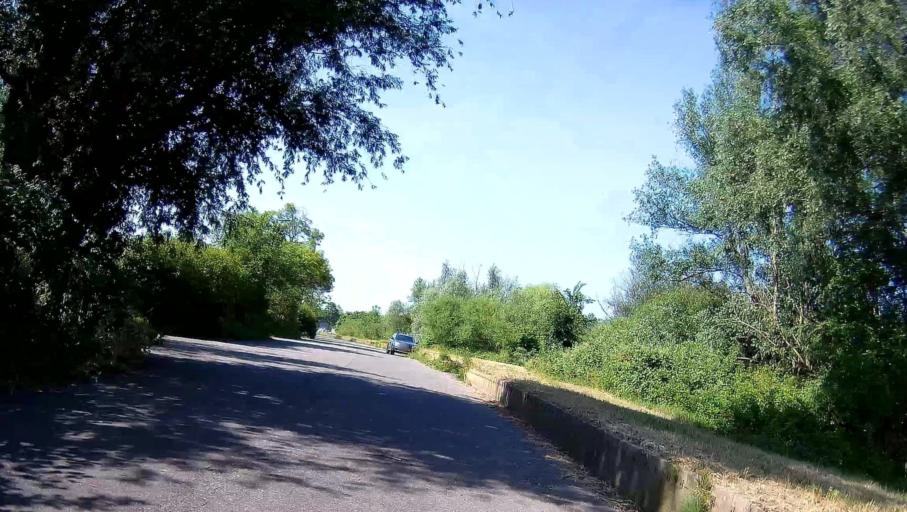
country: NL
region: South Holland
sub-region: Gemeente Schiedam
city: Schiedam
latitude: 51.9366
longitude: 4.4086
